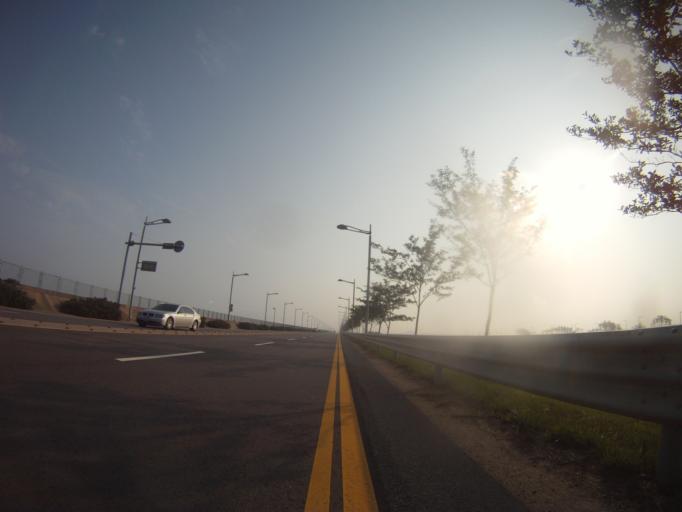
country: KR
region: Incheon
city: Incheon
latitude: 37.4235
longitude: 126.4461
